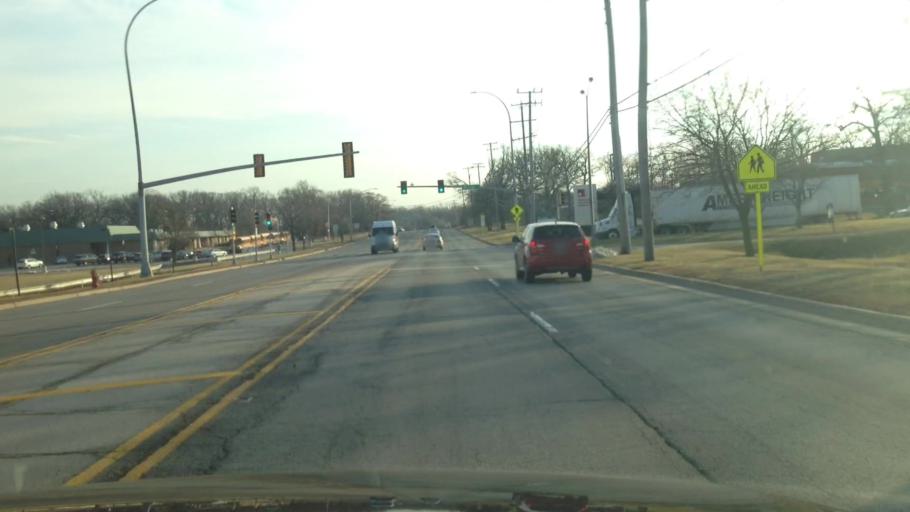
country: US
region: Illinois
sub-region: DuPage County
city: Wood Dale
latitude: 41.9778
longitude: -87.9798
